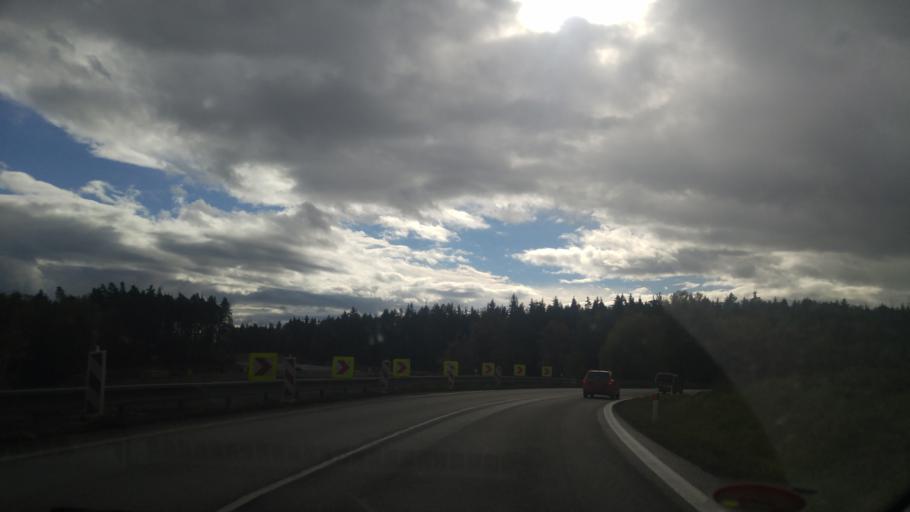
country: CZ
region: Jihocesky
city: Borek
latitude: 49.0300
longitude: 14.5087
